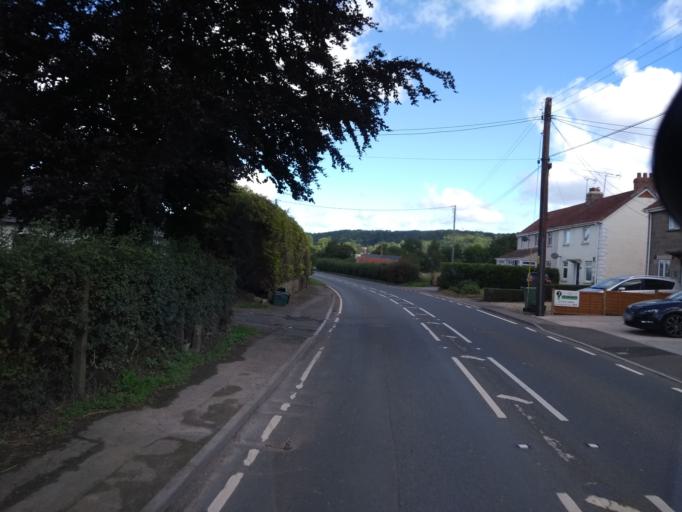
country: GB
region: England
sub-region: Somerset
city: Street
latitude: 51.0974
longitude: -2.7339
